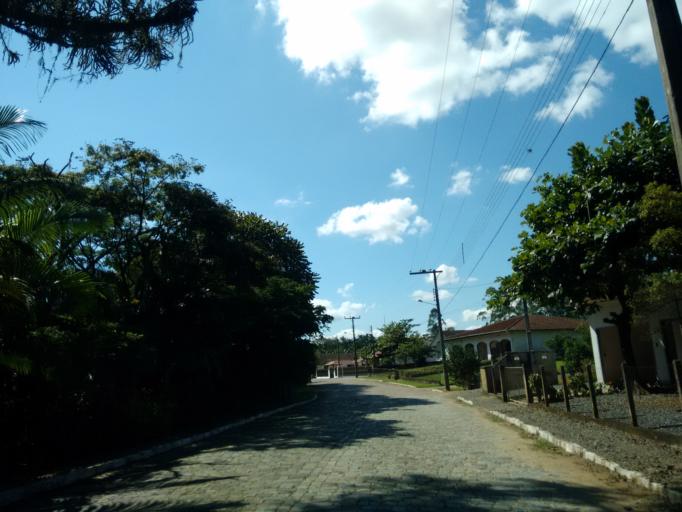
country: BR
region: Santa Catarina
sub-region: Indaial
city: Indaial
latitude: -26.8965
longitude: -49.1919
